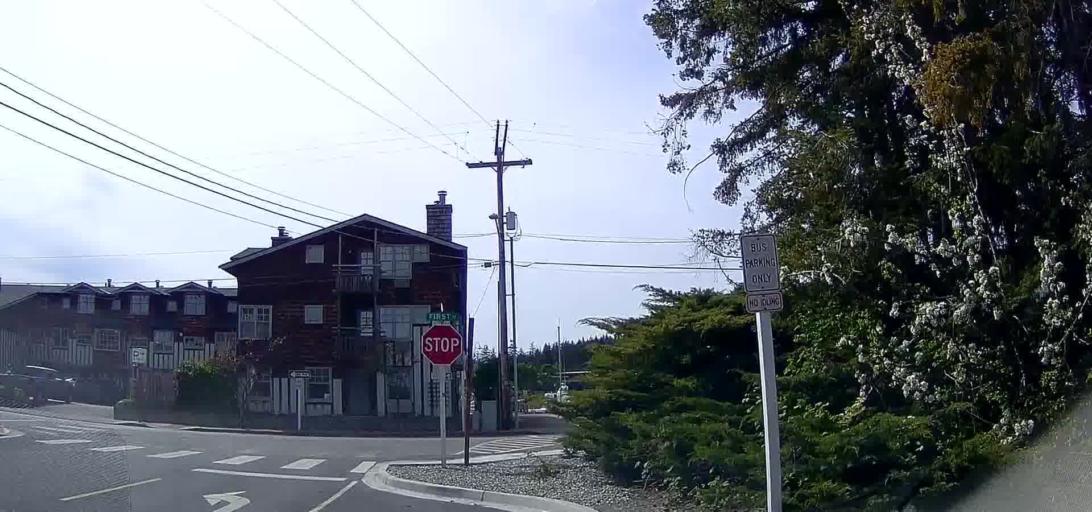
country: US
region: Washington
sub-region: Skagit County
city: Mount Vernon
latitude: 48.3937
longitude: -122.4955
